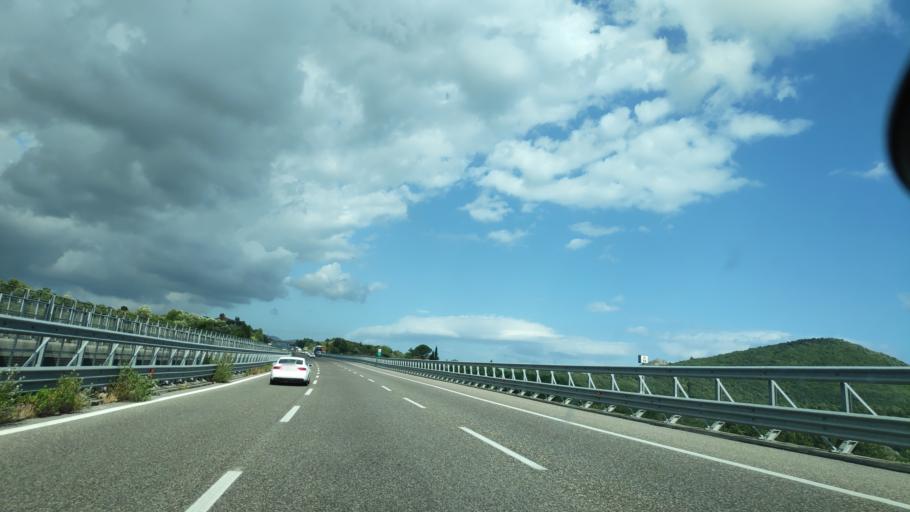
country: IT
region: Campania
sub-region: Provincia di Salerno
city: Contursi Terme
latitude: 40.6125
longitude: 15.2559
